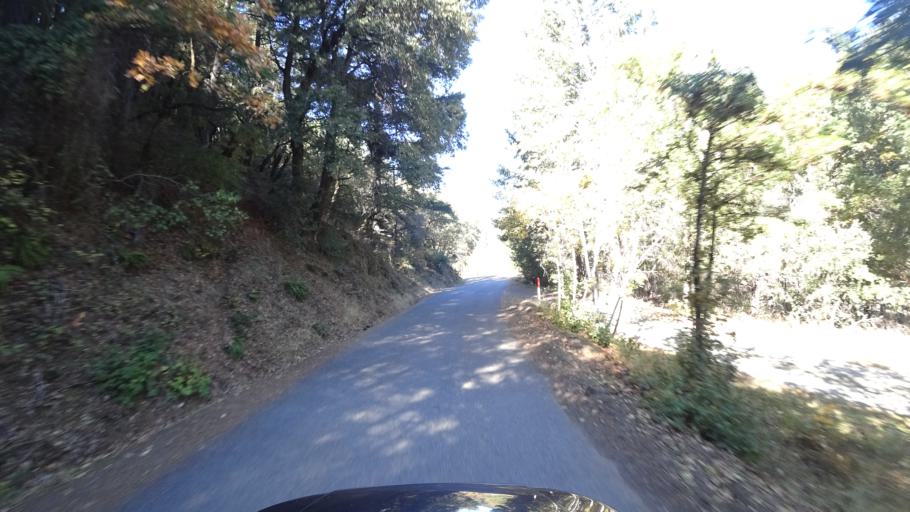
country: US
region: California
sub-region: Humboldt County
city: Willow Creek
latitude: 41.2487
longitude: -123.3035
